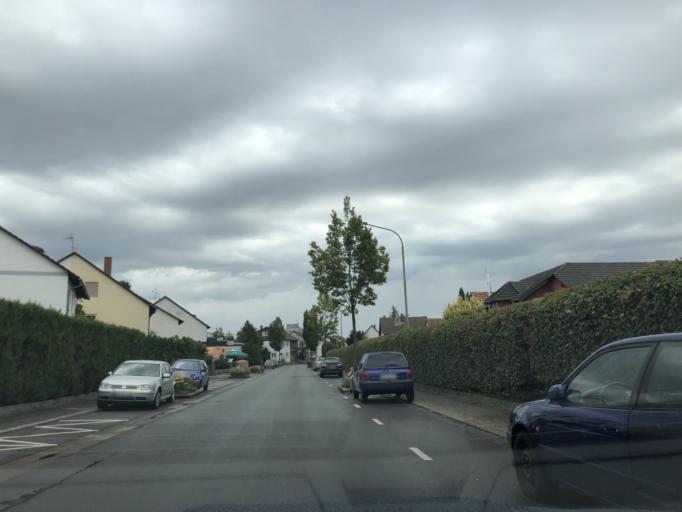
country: DE
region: Rheinland-Pfalz
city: Bellheim
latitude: 49.1975
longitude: 8.2895
